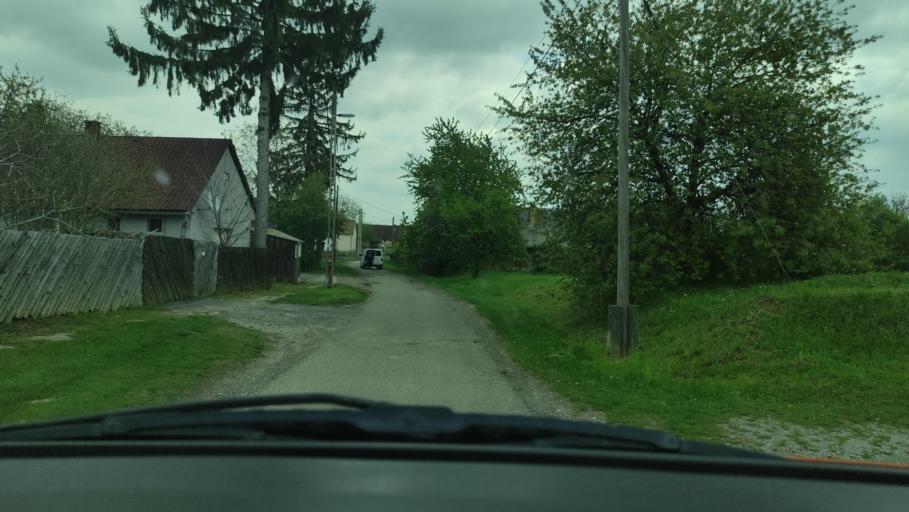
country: HU
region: Somogy
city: Taszar
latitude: 46.2968
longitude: 17.9736
